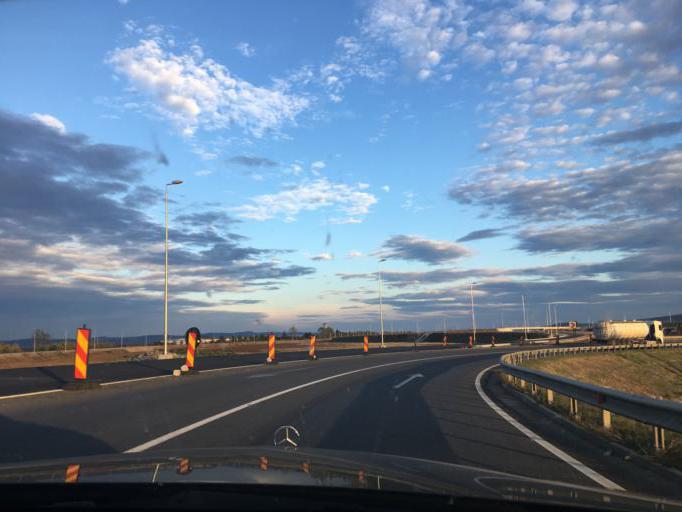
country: RO
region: Cluj
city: Turda
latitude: 46.5296
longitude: 23.7913
